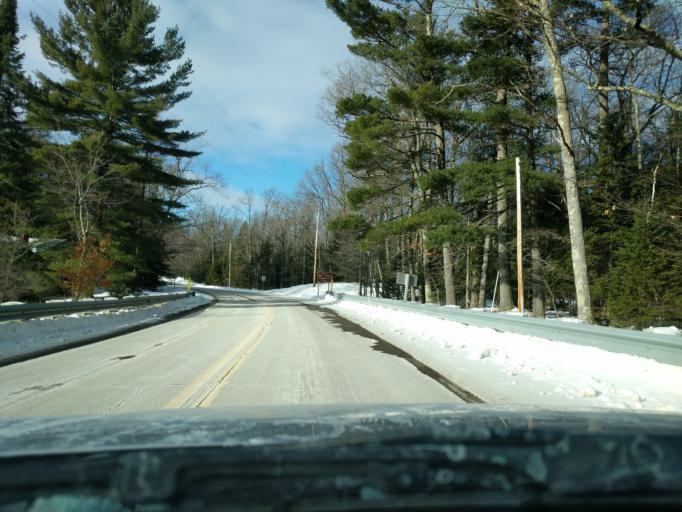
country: US
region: Wisconsin
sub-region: Vilas County
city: Eagle River
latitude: 45.7810
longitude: -89.0741
